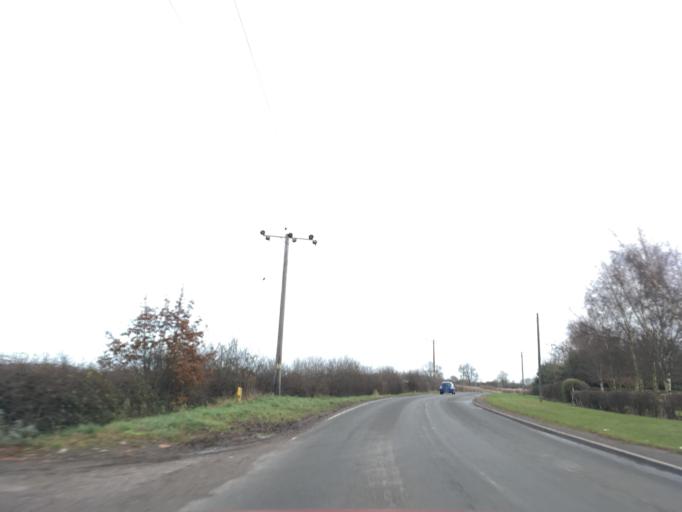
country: GB
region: England
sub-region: Nottinghamshire
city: Ruddington
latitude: 52.8920
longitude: -1.1397
